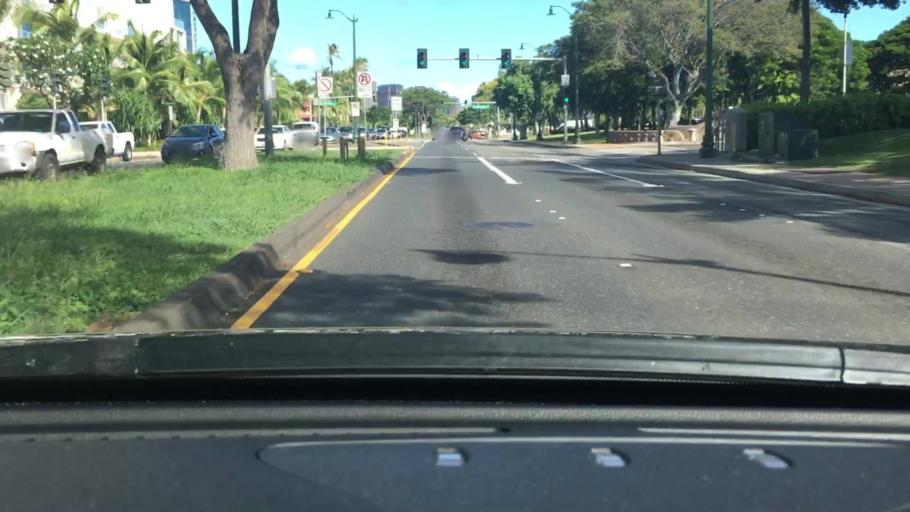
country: US
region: Hawaii
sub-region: Honolulu County
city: Honolulu
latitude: 21.2937
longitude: -157.8552
